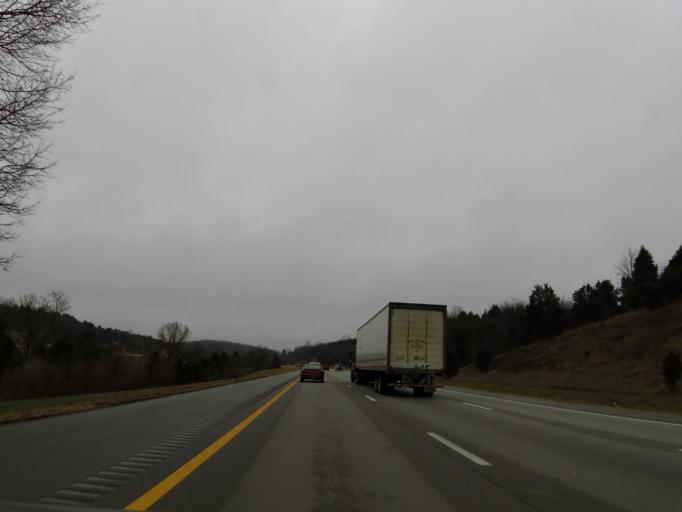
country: US
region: Kentucky
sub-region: Scott County
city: Georgetown
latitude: 38.3399
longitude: -84.5685
